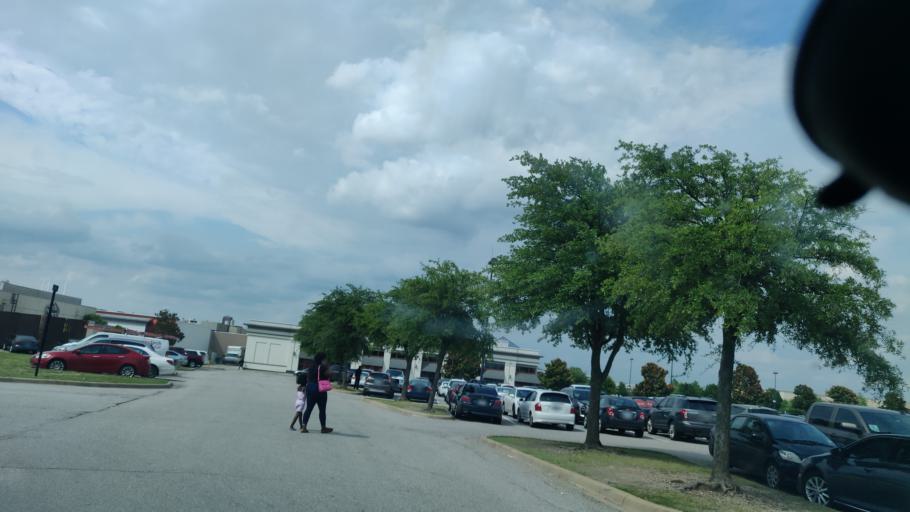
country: US
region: Texas
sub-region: Dallas County
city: Sachse
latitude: 32.9504
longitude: -96.6131
